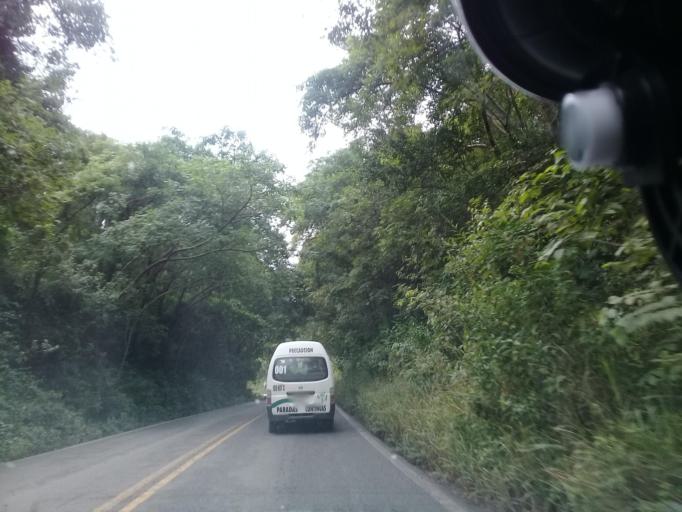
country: MX
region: Hidalgo
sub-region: Huejutla de Reyes
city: Parque de Poblamiento Solidaridad
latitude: 21.1963
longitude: -98.3905
